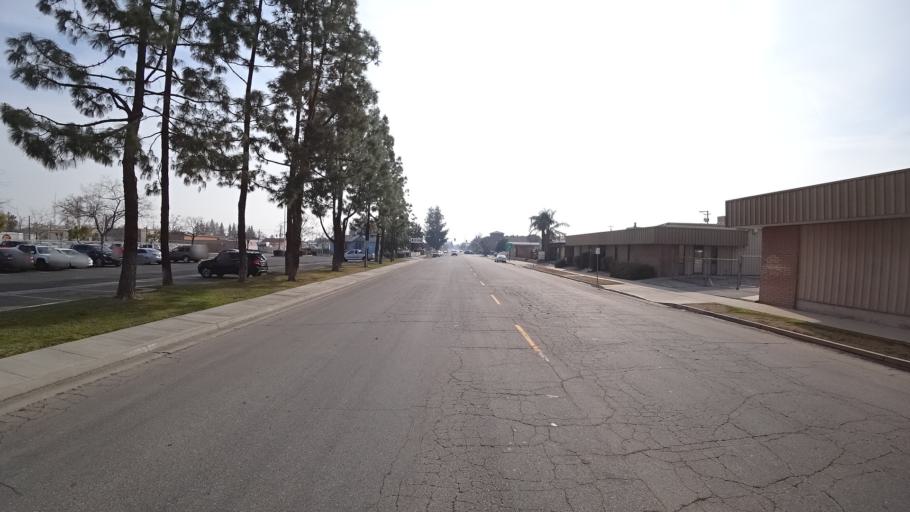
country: US
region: California
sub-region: Kern County
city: Bakersfield
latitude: 35.3826
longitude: -119.0152
